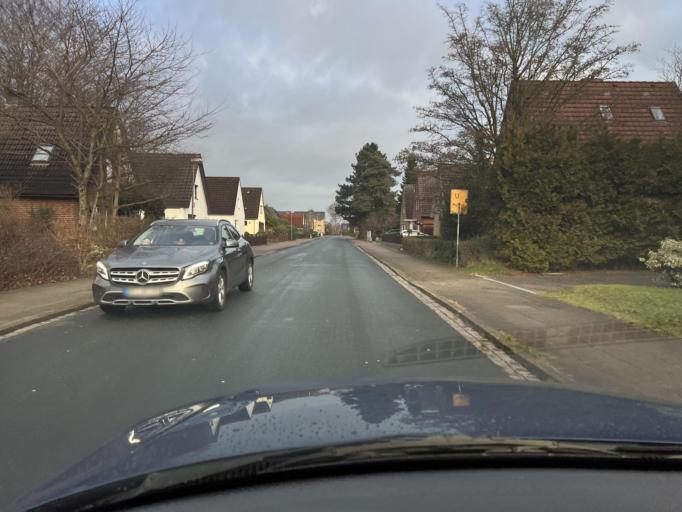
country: DE
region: Schleswig-Holstein
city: Heide
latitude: 54.2023
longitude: 9.0968
